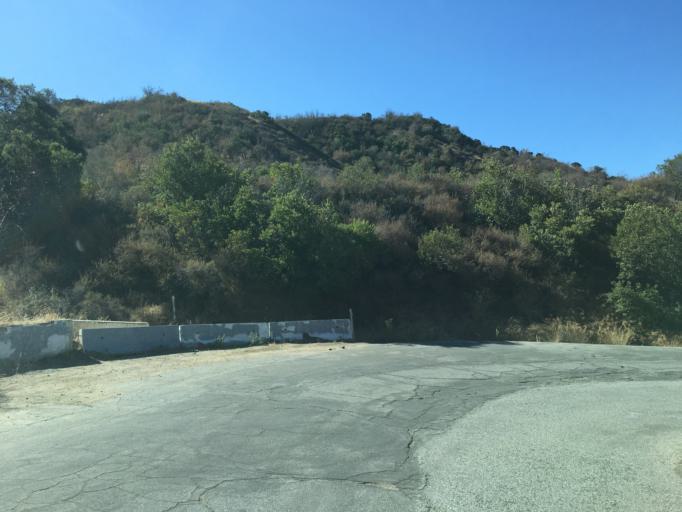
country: US
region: California
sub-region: Los Angeles County
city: La Verne
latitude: 34.1542
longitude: -117.7711
